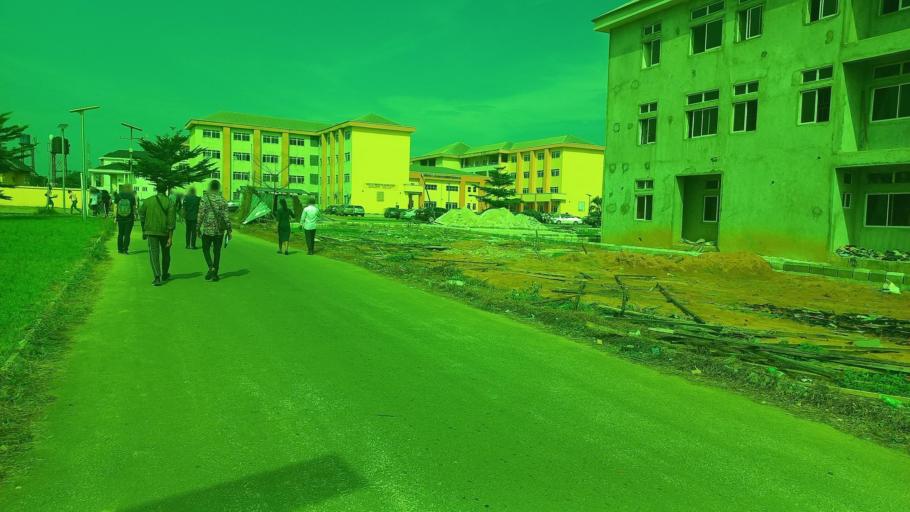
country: NG
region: Rivers
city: Port Harcourt
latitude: 4.7996
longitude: 6.9799
